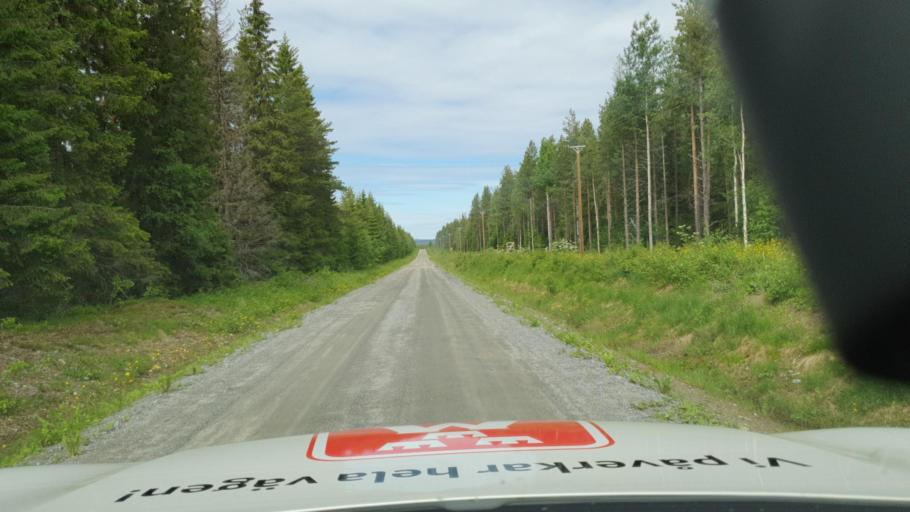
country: SE
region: Vaesterbotten
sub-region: Skelleftea Kommun
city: Langsele
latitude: 64.6012
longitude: 20.2871
